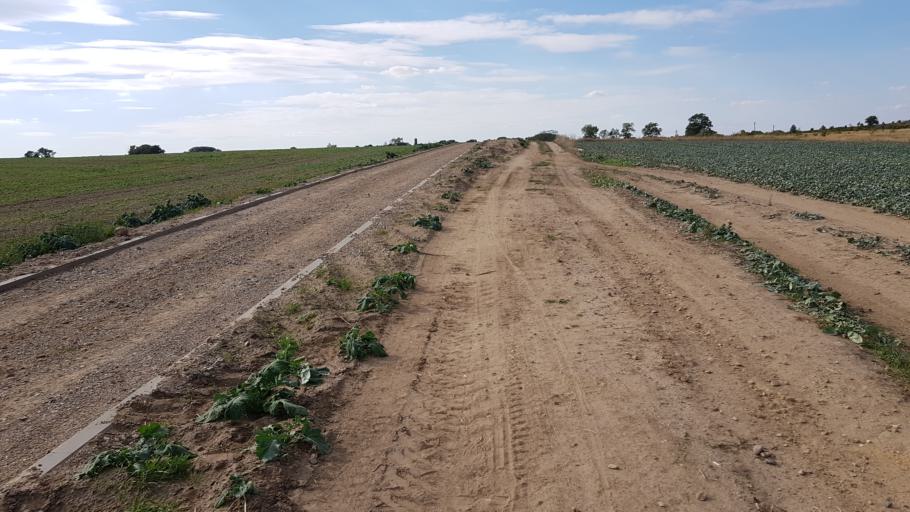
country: PL
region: West Pomeranian Voivodeship
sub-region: Powiat policki
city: Kolbaskowo
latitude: 53.3791
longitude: 14.4185
